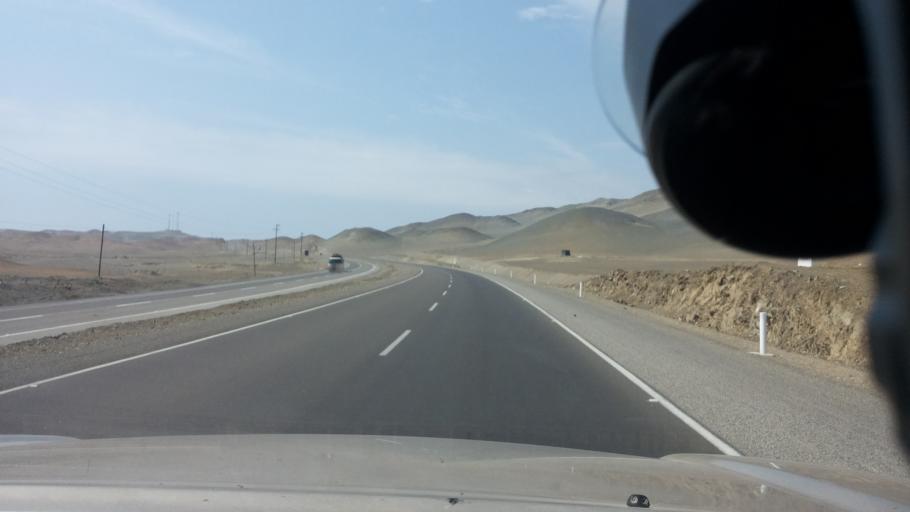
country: PE
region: Ancash
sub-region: Provincia de Huarmey
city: La Caleta Culebras
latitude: -9.9719
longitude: -78.2016
